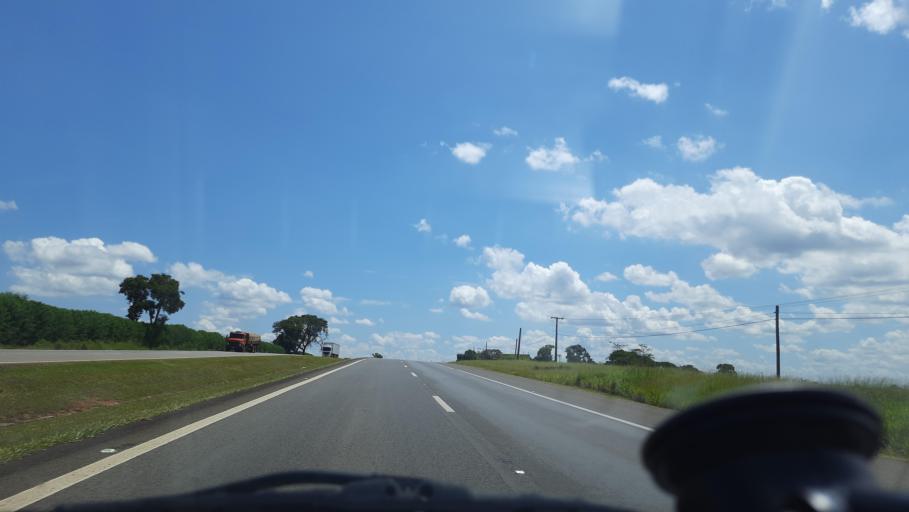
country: BR
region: Sao Paulo
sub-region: Moji-Guacu
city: Mogi-Gaucu
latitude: -22.2577
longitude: -46.9767
